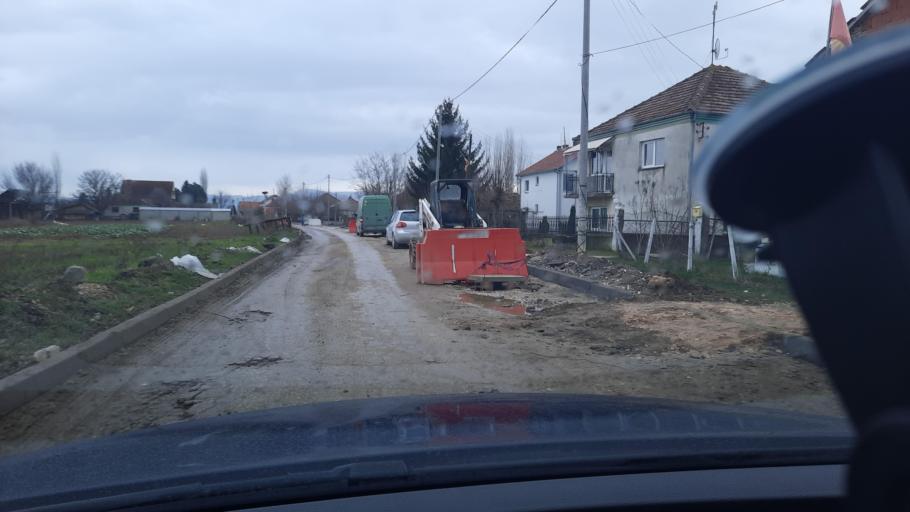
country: MK
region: Mogila
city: Mogila
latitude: 41.1100
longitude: 21.3838
